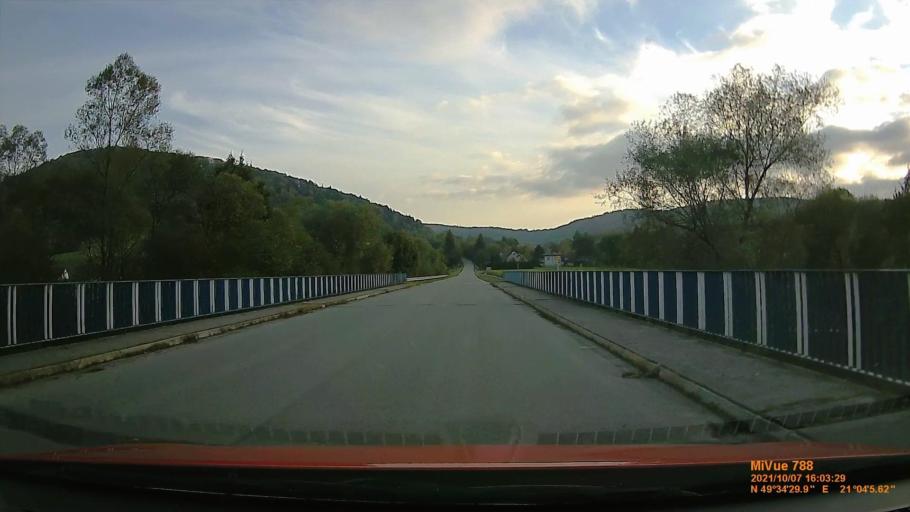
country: PL
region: Lesser Poland Voivodeship
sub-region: Powiat gorlicki
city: Ropa
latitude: 49.5750
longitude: 21.0683
